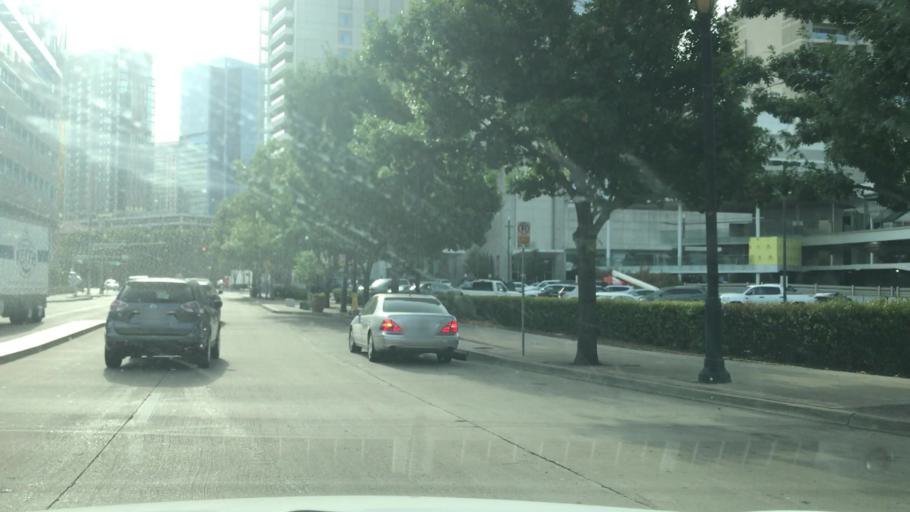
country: US
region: Texas
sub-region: Dallas County
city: Dallas
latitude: 32.7888
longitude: -96.8107
